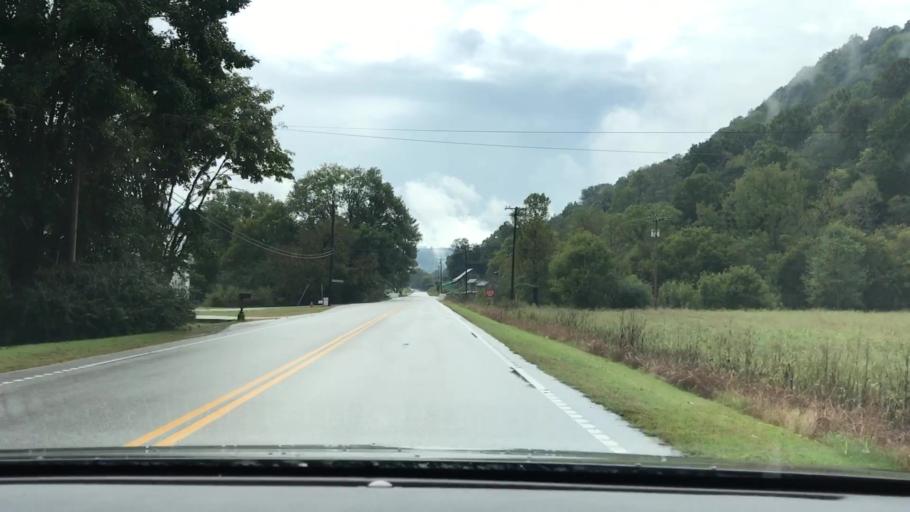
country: US
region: Tennessee
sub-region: Smith County
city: Carthage
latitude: 36.3800
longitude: -85.9495
